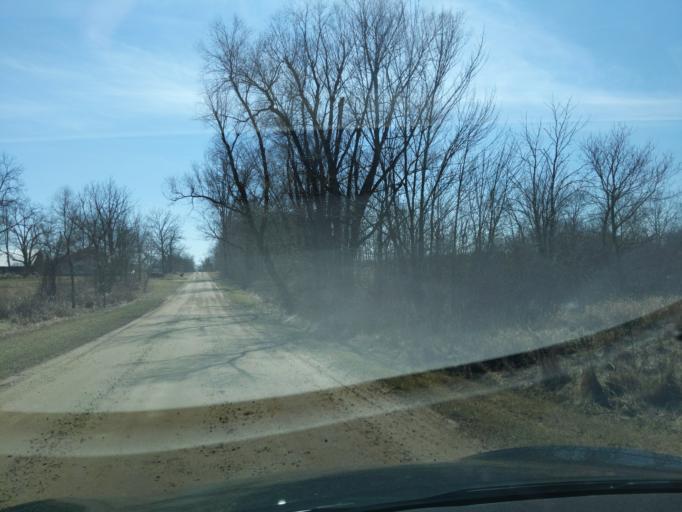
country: US
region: Michigan
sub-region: Ionia County
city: Lake Odessa
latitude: 42.7254
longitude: -85.0539
